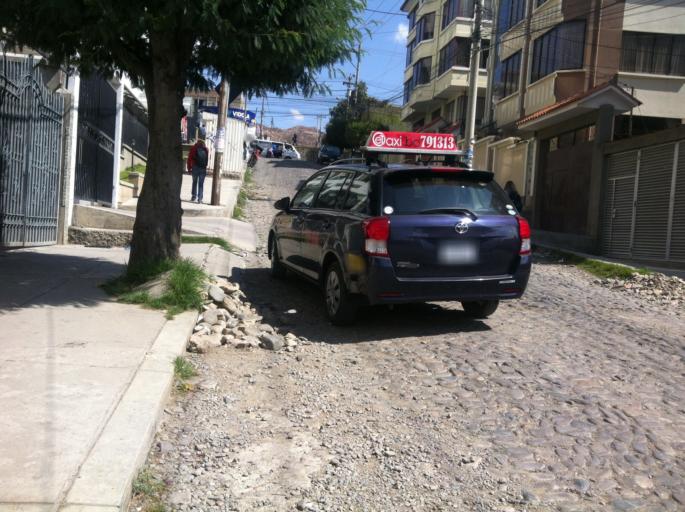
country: BO
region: La Paz
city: La Paz
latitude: -16.5400
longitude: -68.0683
